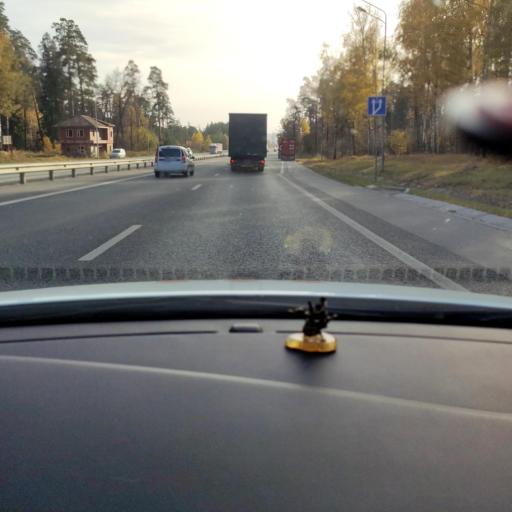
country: RU
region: Tatarstan
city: Osinovo
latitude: 55.8309
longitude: 48.8493
